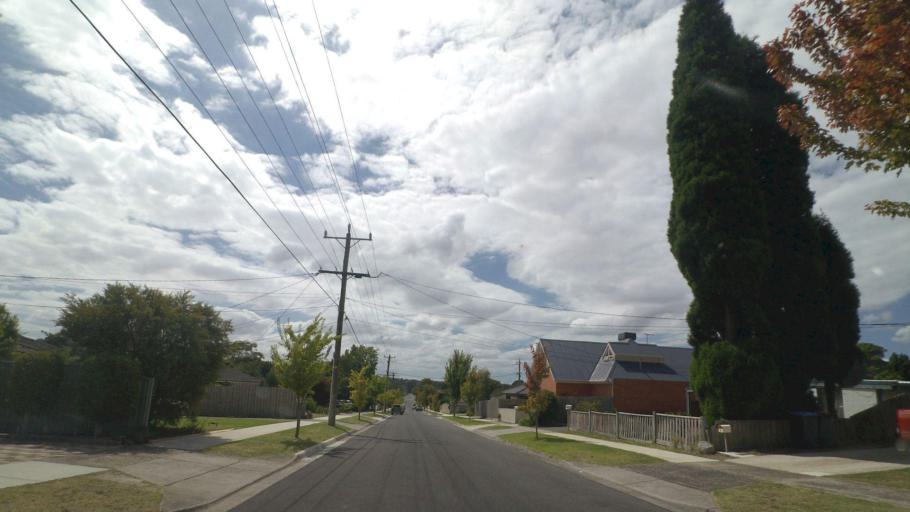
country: AU
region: Victoria
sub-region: Knox
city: Wantirna South
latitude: -37.8832
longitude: 145.2208
